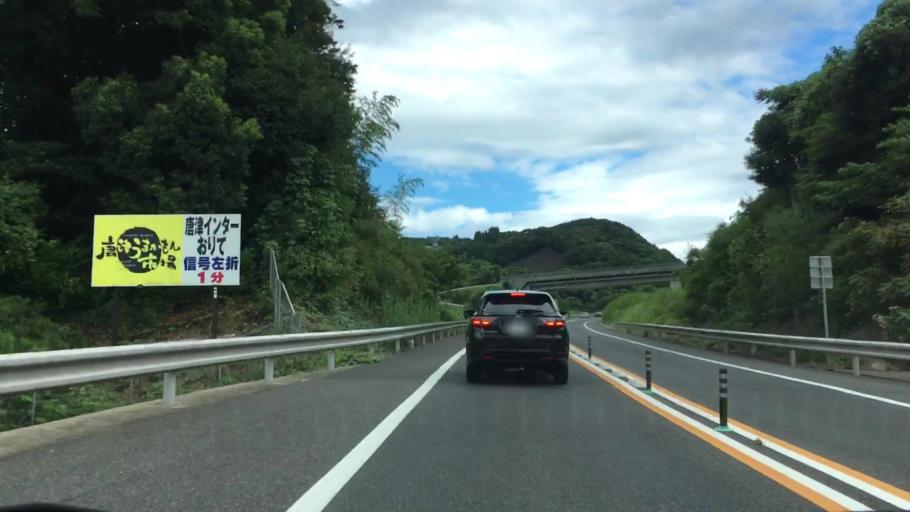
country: JP
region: Saga Prefecture
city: Karatsu
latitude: 33.3954
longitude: 129.9354
